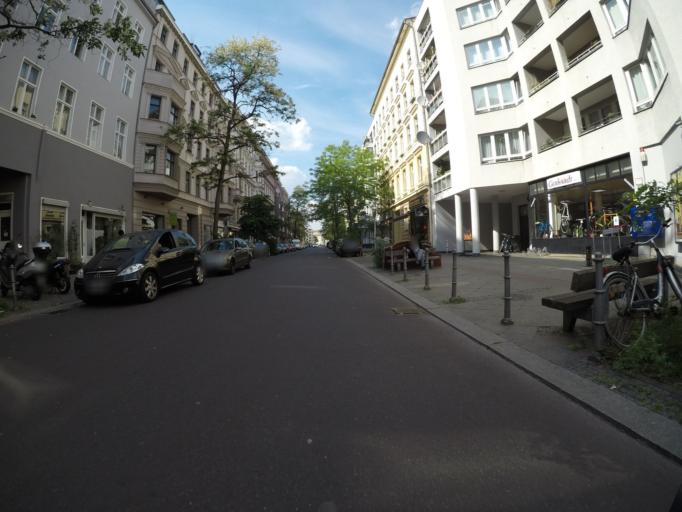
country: DE
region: Berlin
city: Moabit
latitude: 52.5271
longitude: 13.3516
